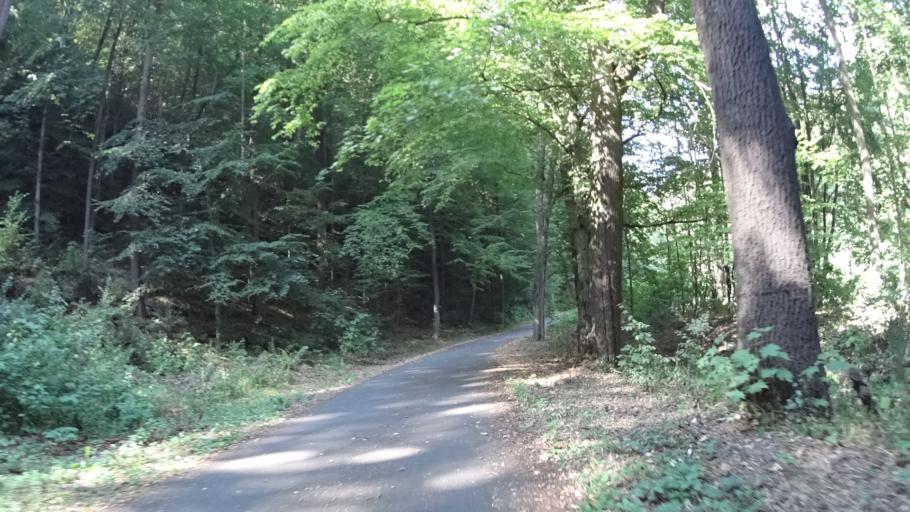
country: DE
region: Saxony
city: Ostritz
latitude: 50.9775
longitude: 14.9183
